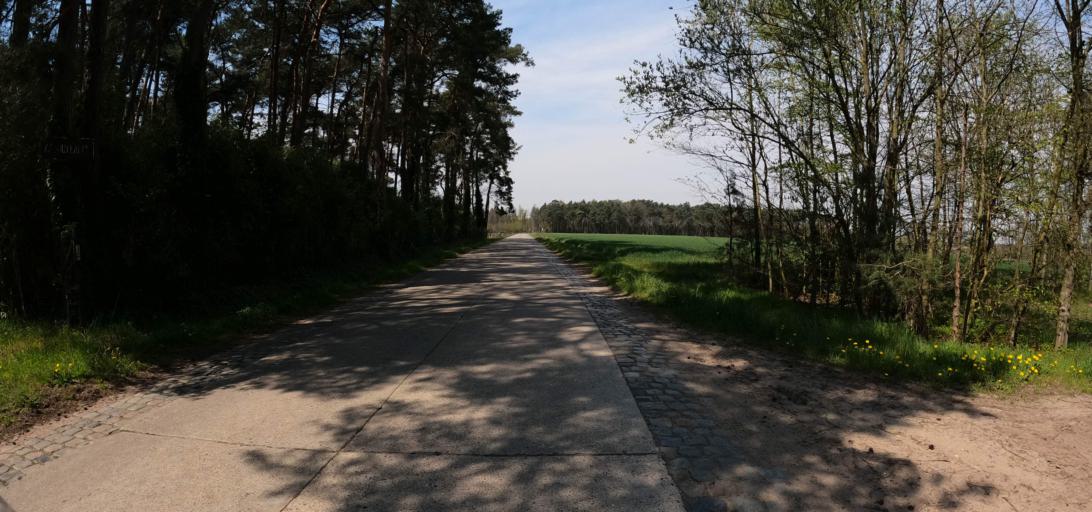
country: BE
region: Flanders
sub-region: Provincie Antwerpen
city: Vorselaar
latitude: 51.2374
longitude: 4.7676
